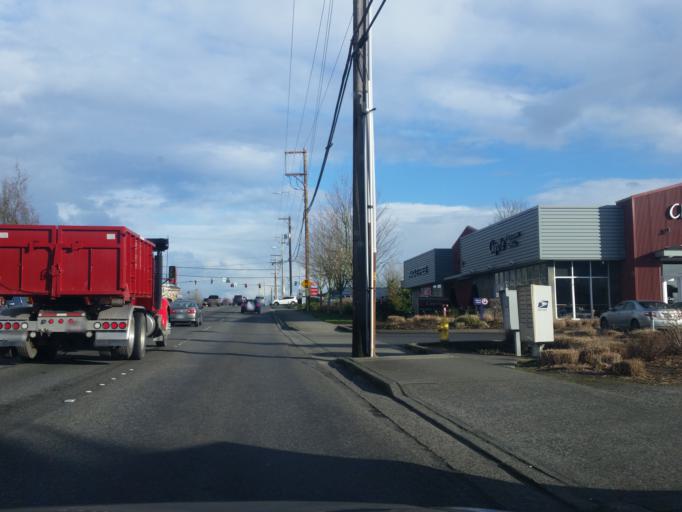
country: US
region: Washington
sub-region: Snohomish County
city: Alderwood Manor
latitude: 47.8209
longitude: -122.2893
